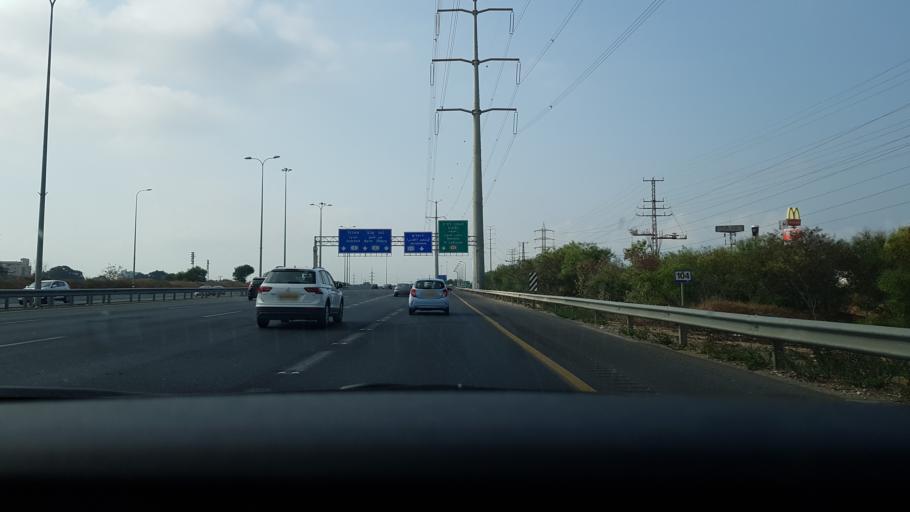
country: IL
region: Central District
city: Rishon LeZiyyon
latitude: 31.9689
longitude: 34.7882
